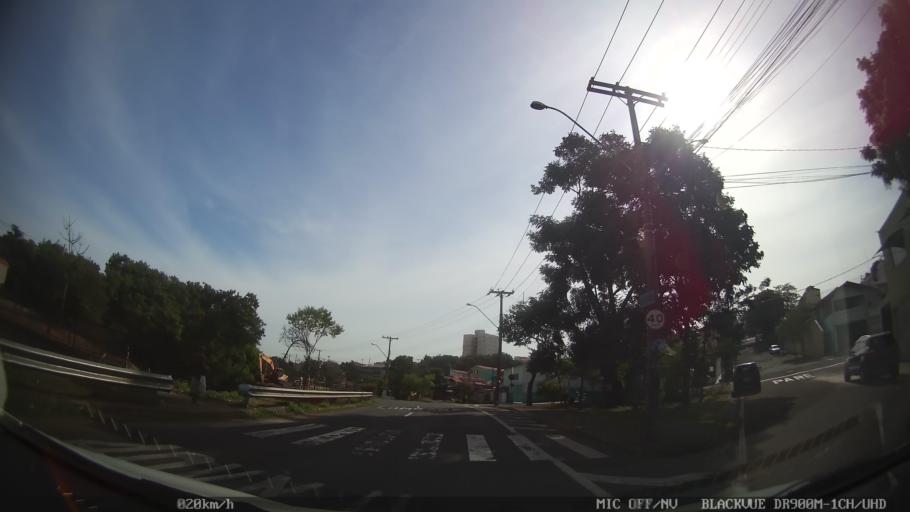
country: BR
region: Sao Paulo
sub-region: Piracicaba
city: Piracicaba
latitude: -22.7351
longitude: -47.6689
